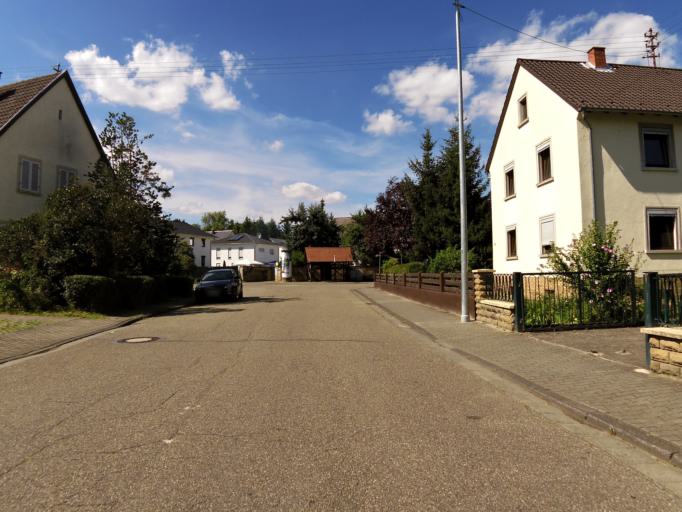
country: DE
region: Rheinland-Pfalz
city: Hanhofen
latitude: 49.3138
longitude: 8.3393
